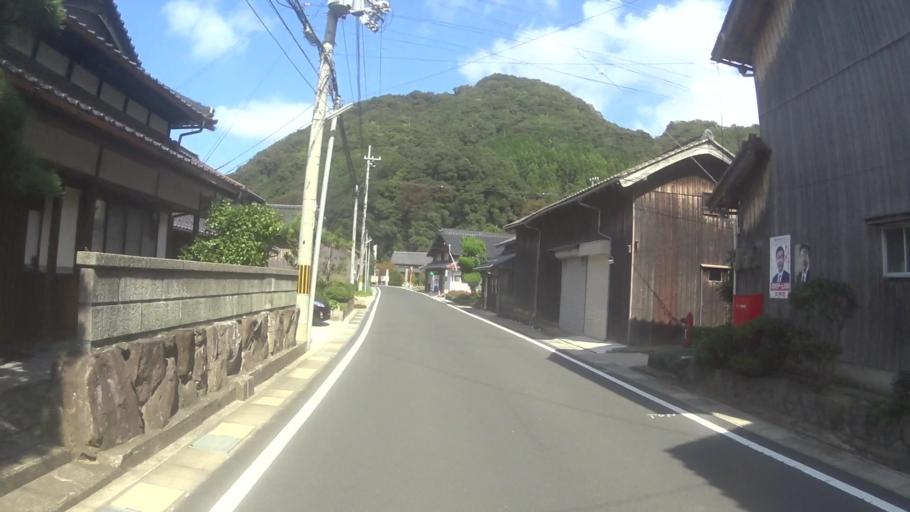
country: JP
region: Kyoto
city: Miyazu
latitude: 35.7359
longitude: 135.1105
